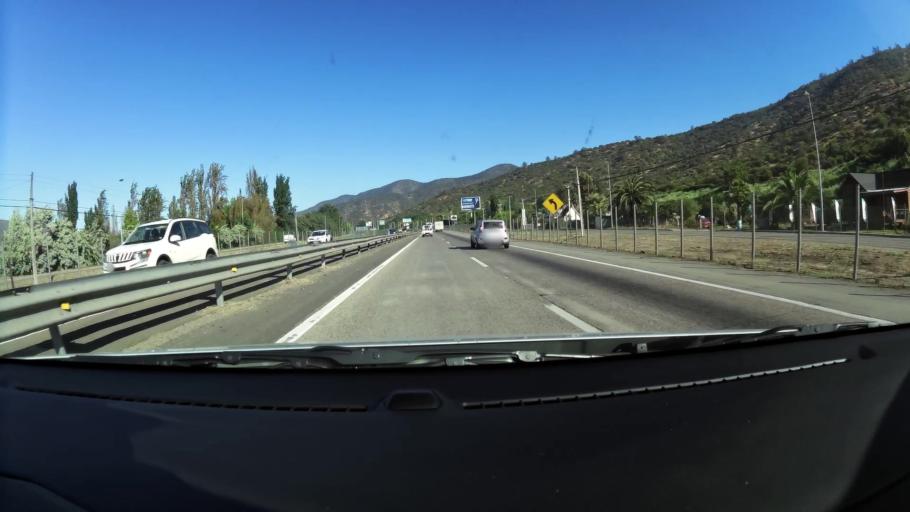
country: CL
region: Santiago Metropolitan
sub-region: Provincia de Chacabuco
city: Lampa
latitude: -33.4147
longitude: -71.0529
